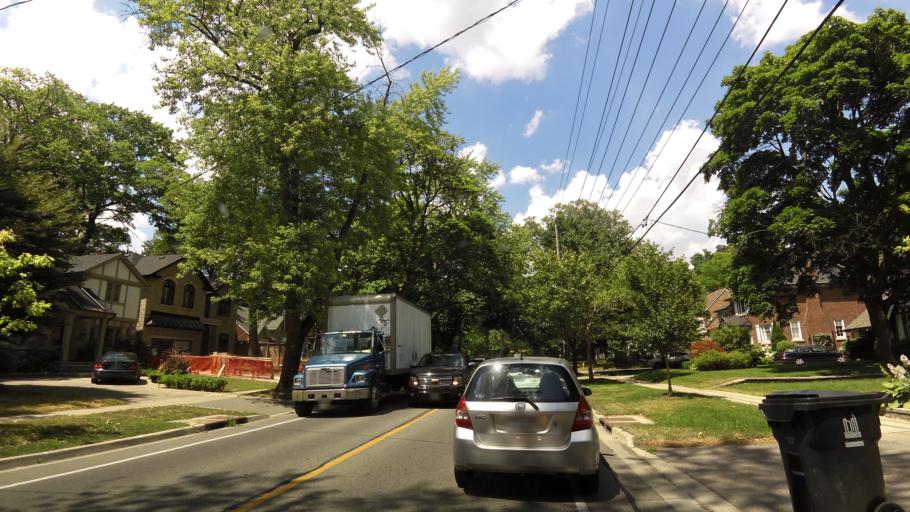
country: CA
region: Ontario
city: Etobicoke
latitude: 43.6521
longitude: -79.5134
